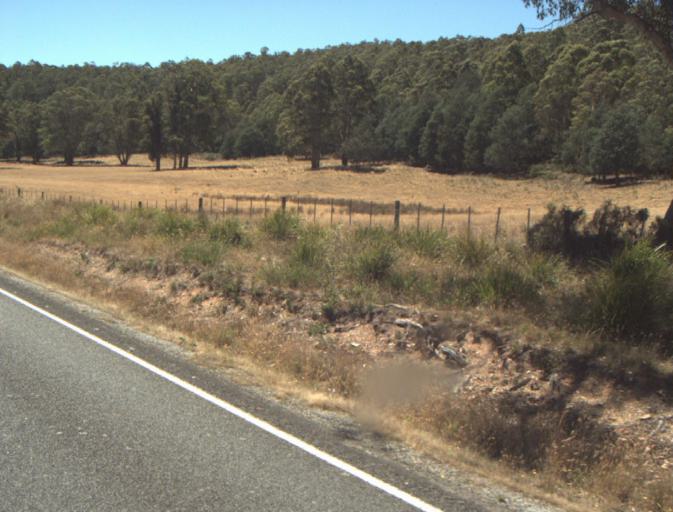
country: AU
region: Tasmania
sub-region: Dorset
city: Scottsdale
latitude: -41.2953
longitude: 147.3852
